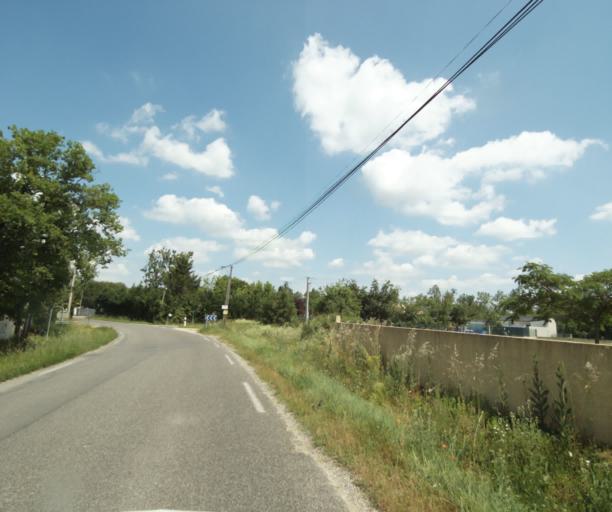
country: FR
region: Midi-Pyrenees
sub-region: Departement du Tarn-et-Garonne
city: Montauban
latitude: 44.0523
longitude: 1.3431
